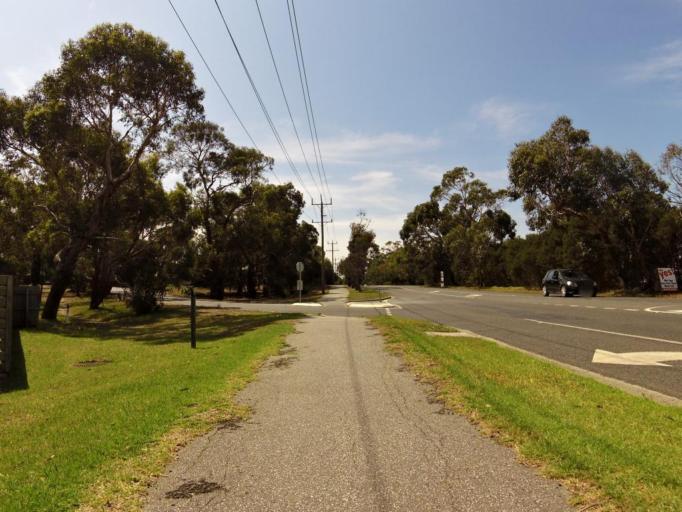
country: AU
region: Victoria
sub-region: Mornington Peninsula
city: Hastings
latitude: -38.2957
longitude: 145.1900
